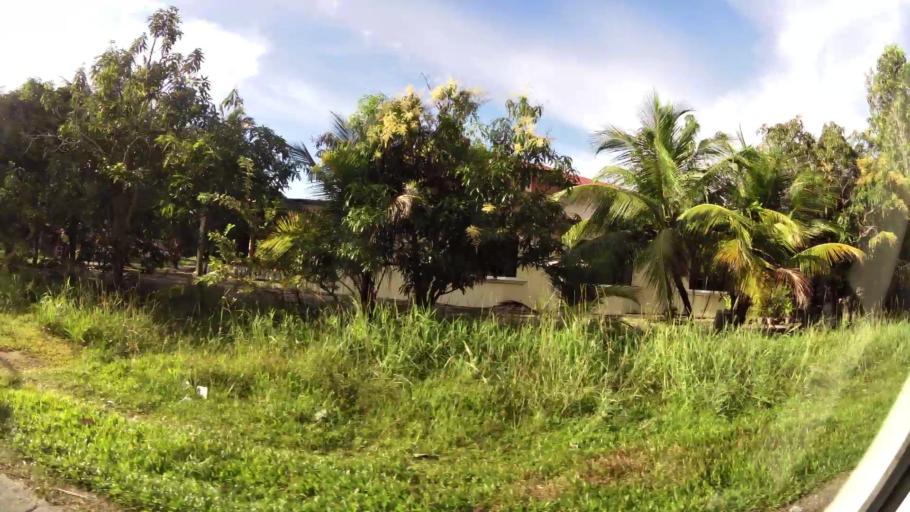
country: BN
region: Brunei and Muara
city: Bandar Seri Begawan
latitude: 4.9809
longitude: 114.9685
